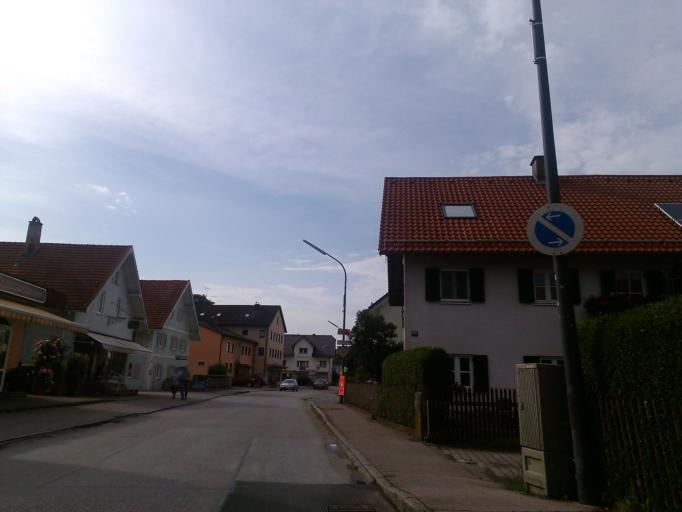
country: DE
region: Bavaria
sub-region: Upper Bavaria
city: Gilching
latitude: 48.1176
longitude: 11.2912
